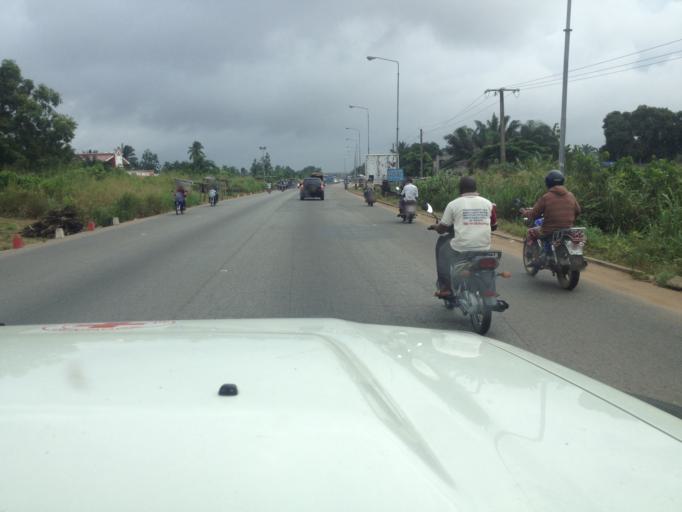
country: BJ
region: Queme
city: Porto-Novo
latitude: 6.4513
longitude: 2.6207
